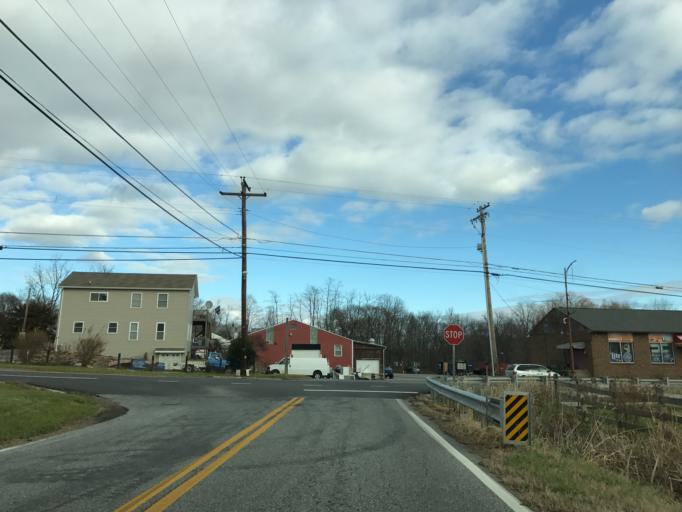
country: US
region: Pennsylvania
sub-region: York County
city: Stewartstown
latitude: 39.6693
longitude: -76.5922
